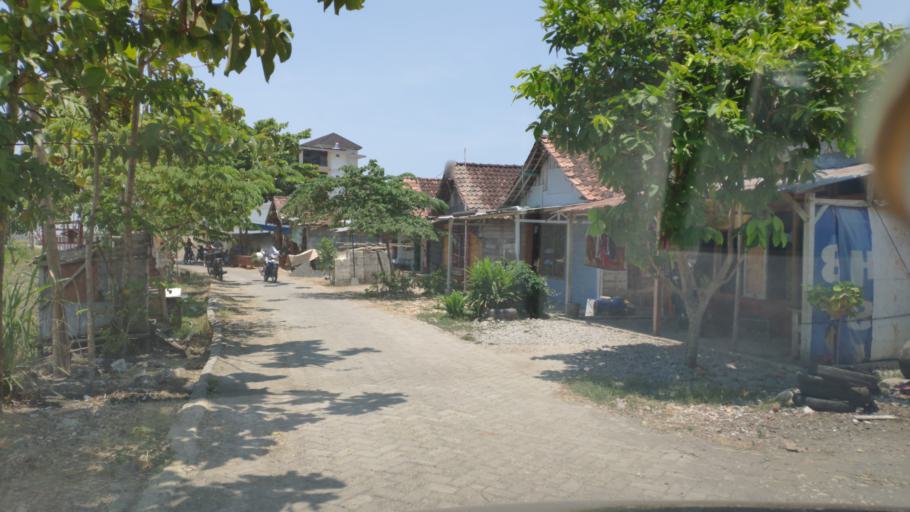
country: ID
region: Central Java
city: Tambakkromo
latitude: -7.1570
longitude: 111.5794
